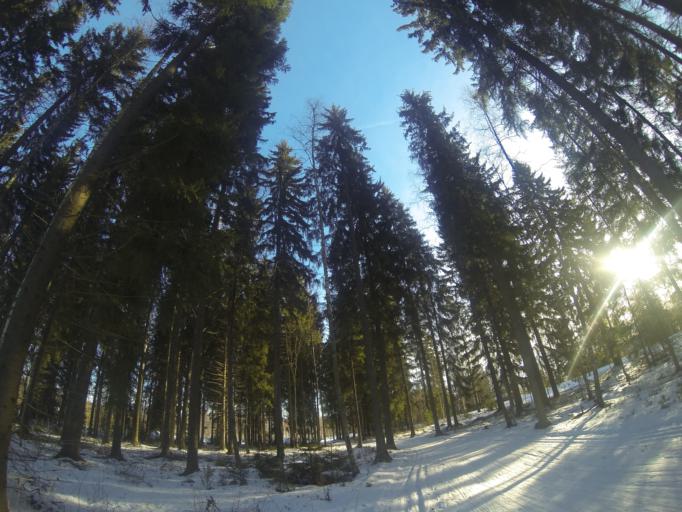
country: FI
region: Southern Savonia
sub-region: Savonlinna
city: Savonlinna
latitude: 61.9175
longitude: 28.9054
